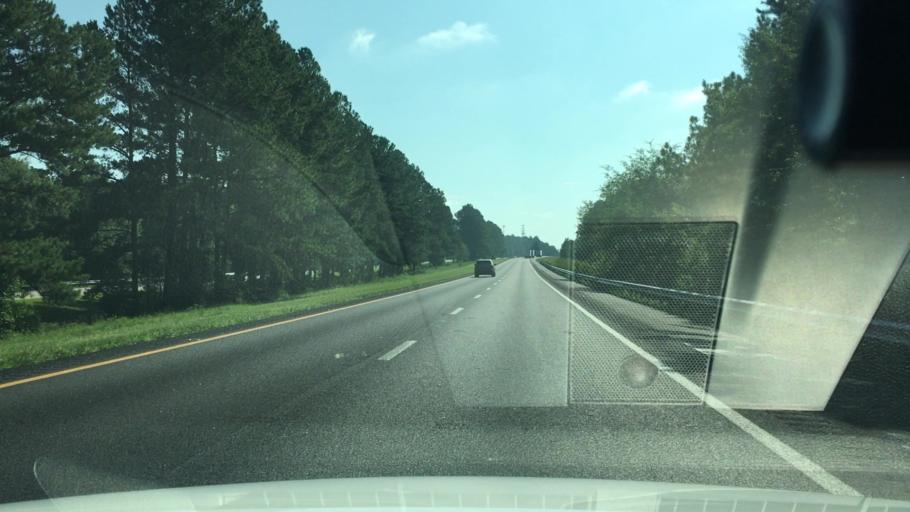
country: US
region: South Carolina
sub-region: Aiken County
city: Graniteville
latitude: 33.6310
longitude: -81.7959
